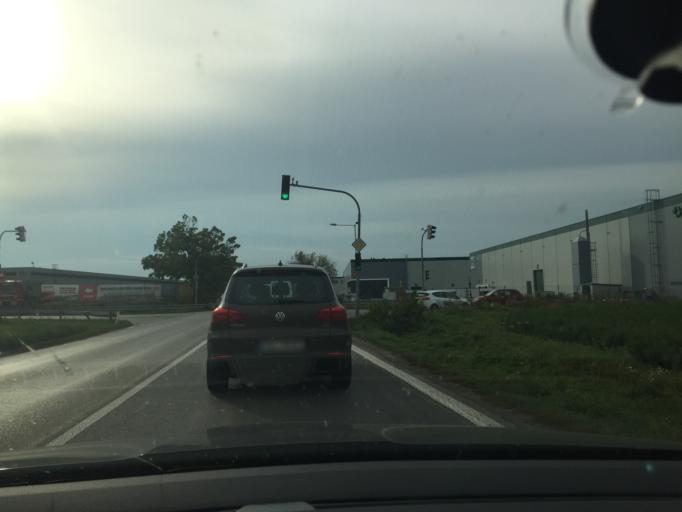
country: CZ
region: Central Bohemia
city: Jirny
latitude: 50.1265
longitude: 14.6998
